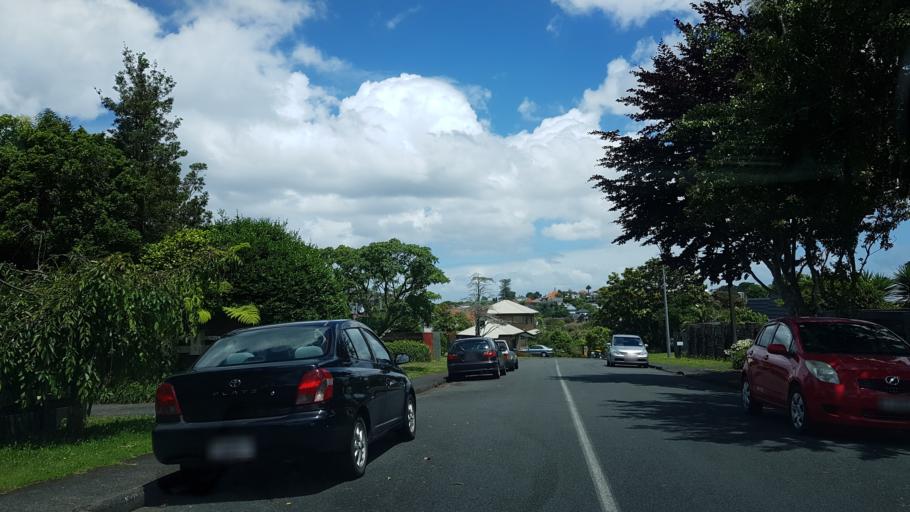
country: NZ
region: Auckland
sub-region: Auckland
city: North Shore
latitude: -36.8033
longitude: 174.7400
